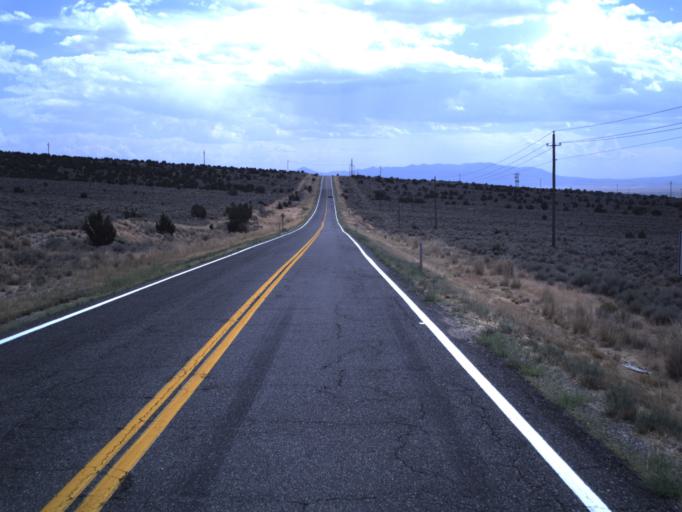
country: US
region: Utah
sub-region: Tooele County
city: Tooele
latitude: 40.3235
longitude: -112.2878
